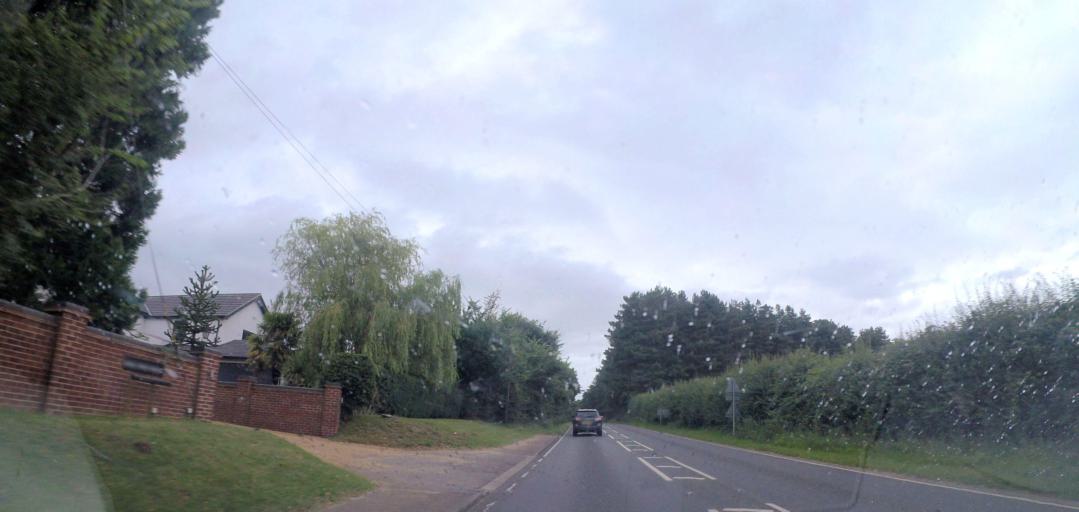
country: GB
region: England
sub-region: Norfolk
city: Spixworth
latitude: 52.7002
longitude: 1.3429
